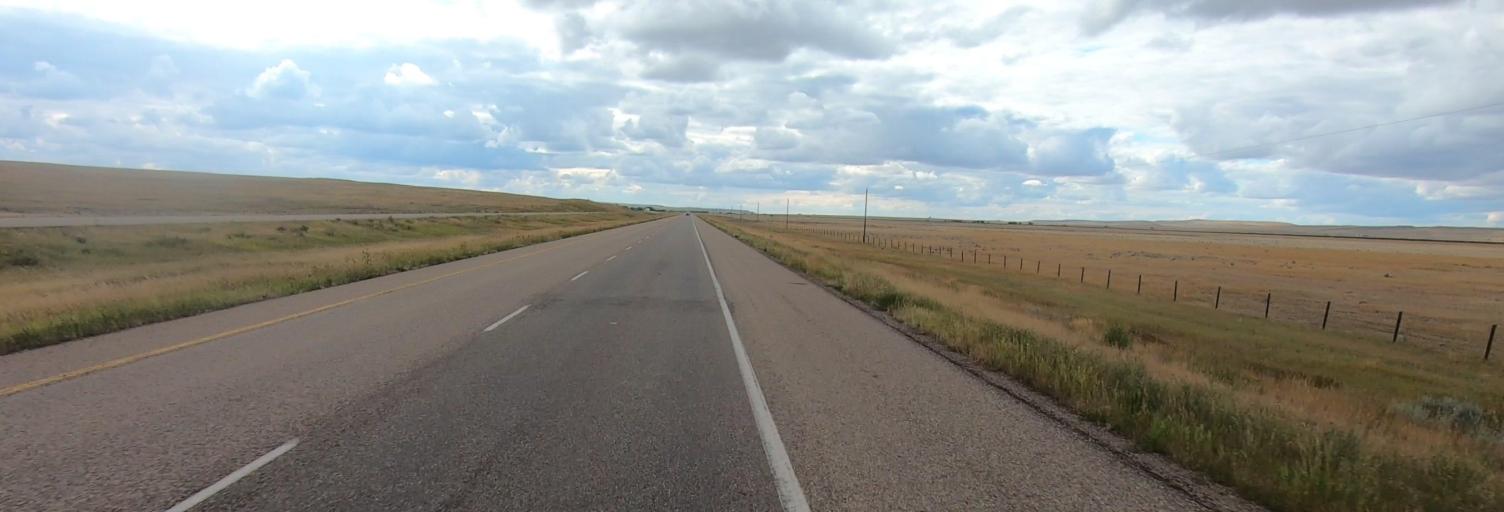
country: CA
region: Alberta
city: Medicine Hat
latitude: 49.9406
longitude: -110.1068
